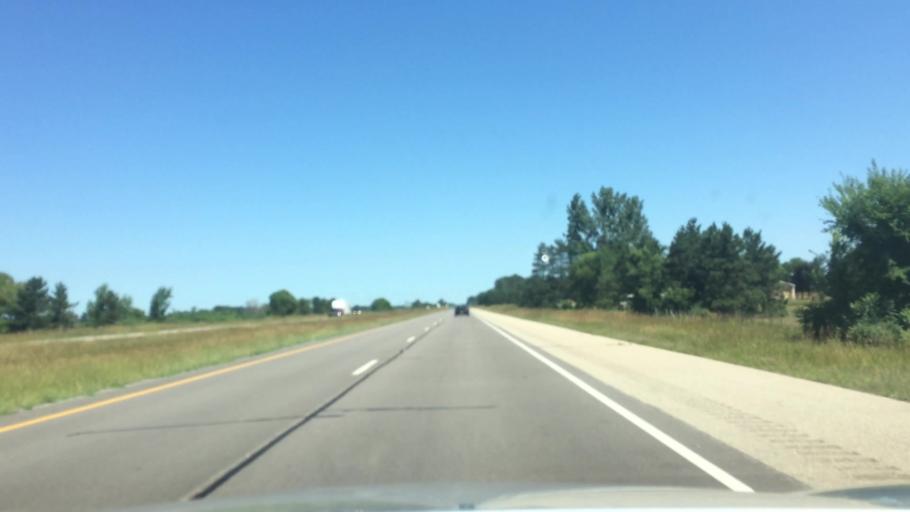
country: US
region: Wisconsin
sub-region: Portage County
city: Plover
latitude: 44.2279
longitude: -89.5245
